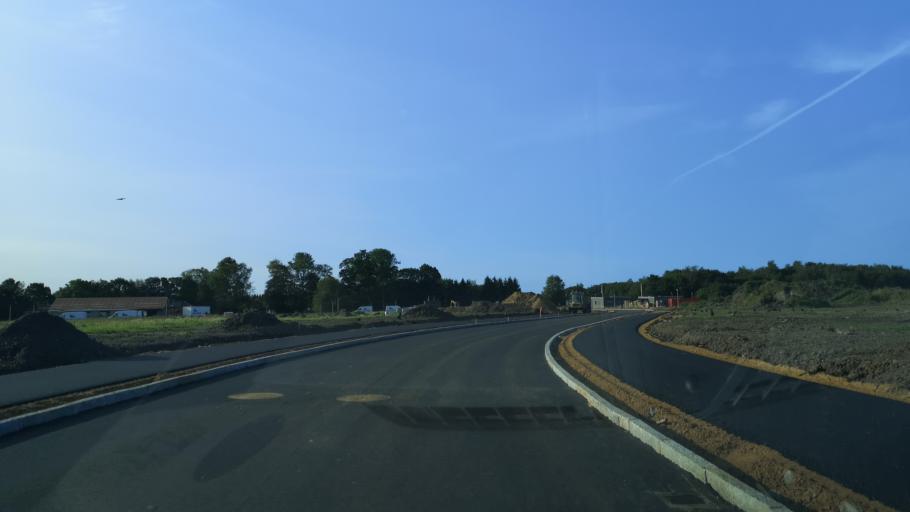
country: DK
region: Central Jutland
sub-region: Herning Kommune
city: Snejbjerg
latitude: 56.1408
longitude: 8.9207
